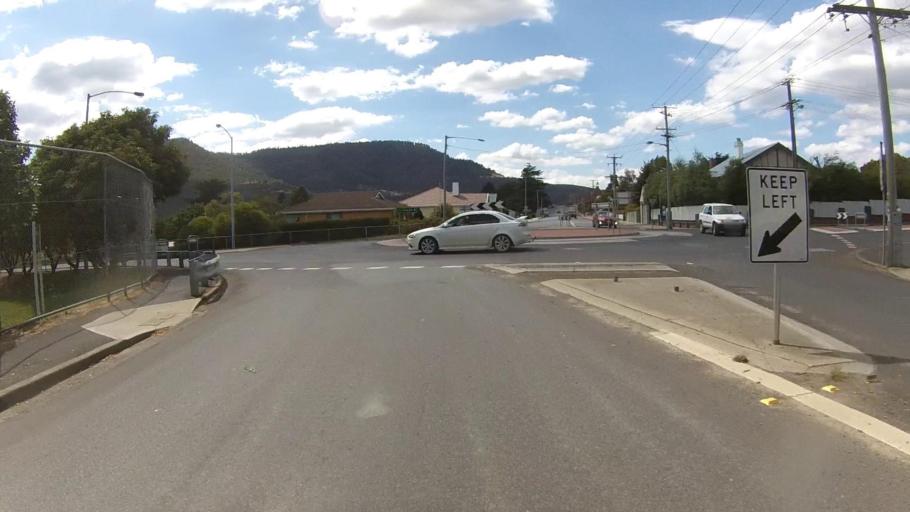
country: AU
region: Tasmania
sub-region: Derwent Valley
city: New Norfolk
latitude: -42.7807
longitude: 147.0566
